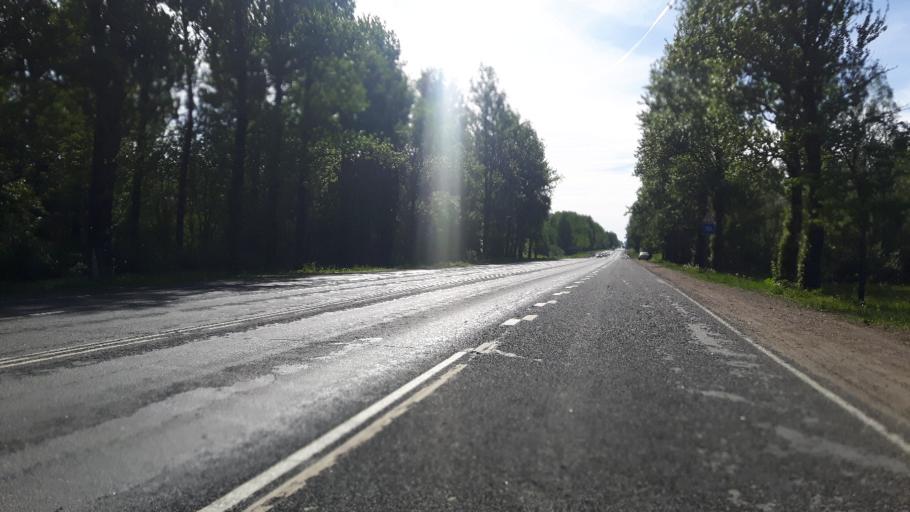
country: RU
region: Leningrad
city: Ivangorod
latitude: 59.3811
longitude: 28.3330
